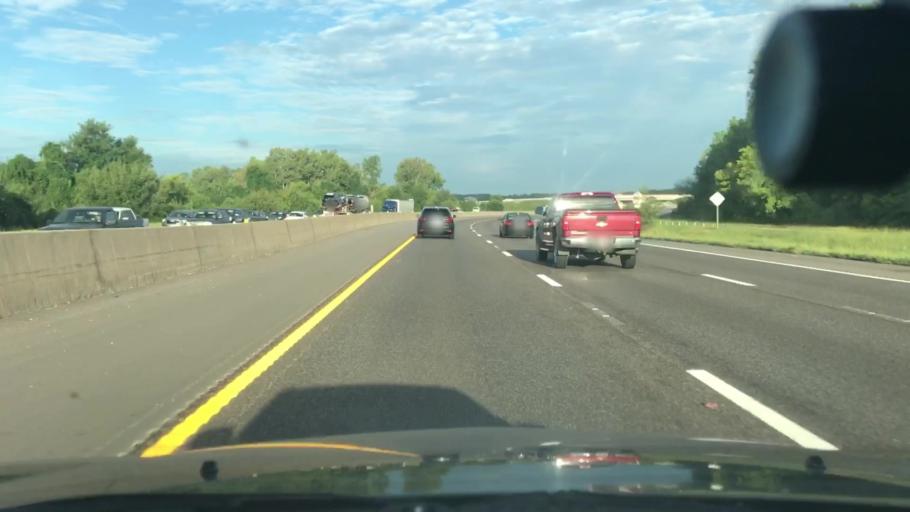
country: US
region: Missouri
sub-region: Saint Charles County
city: Weldon Spring
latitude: 38.6761
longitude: -90.6515
